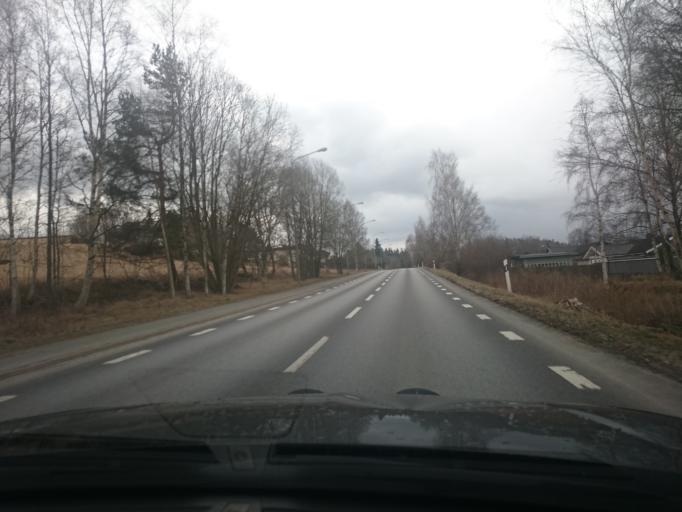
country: SE
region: Joenkoeping
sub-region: Vetlanda Kommun
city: Vetlanda
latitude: 57.2991
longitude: 15.1271
